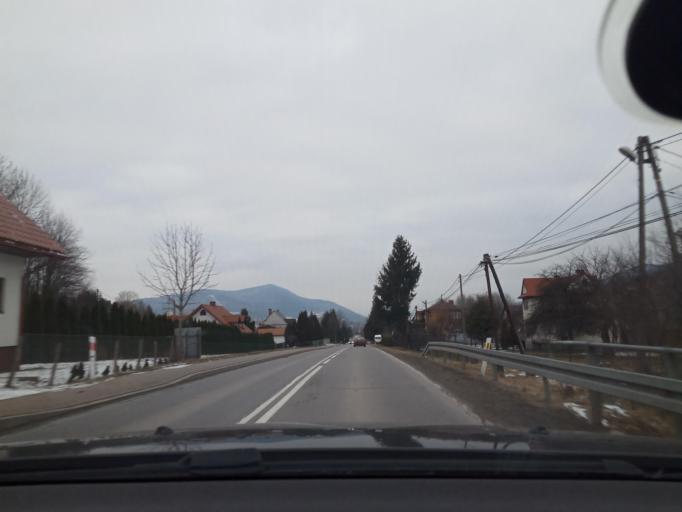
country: PL
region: Lesser Poland Voivodeship
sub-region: Powiat limanowski
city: Mszana Gorna
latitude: 49.6583
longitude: 20.1040
